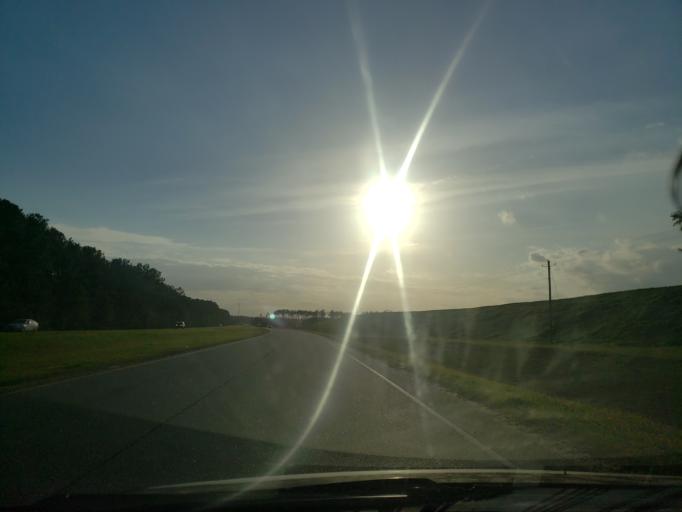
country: US
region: Georgia
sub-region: Chatham County
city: Bloomingdale
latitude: 32.1598
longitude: -81.2696
